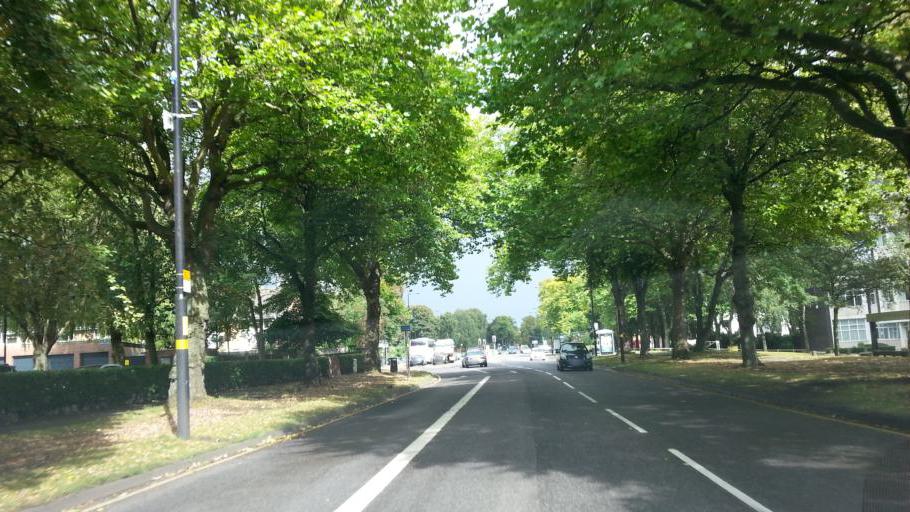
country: GB
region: England
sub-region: City and Borough of Birmingham
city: Birmingham
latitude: 52.4539
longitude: -1.9080
